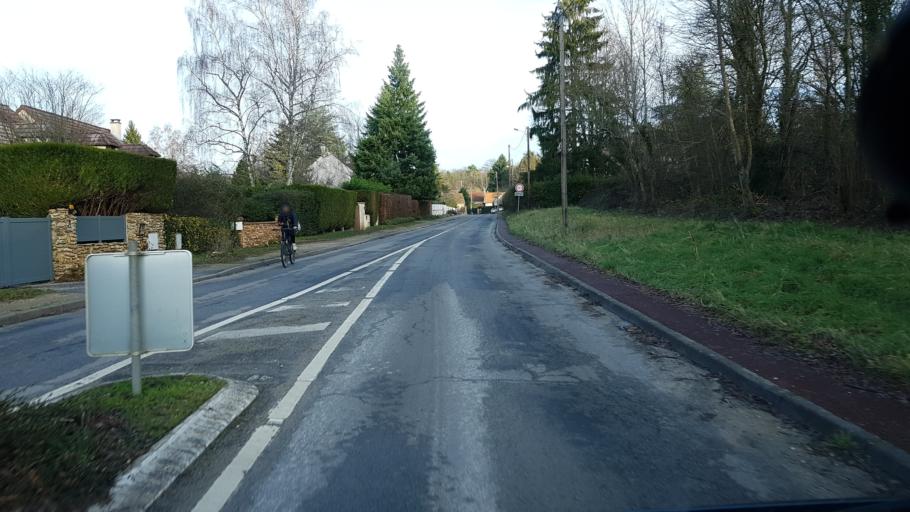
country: FR
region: Ile-de-France
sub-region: Departement des Yvelines
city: Gazeran
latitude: 48.6724
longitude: 1.7453
